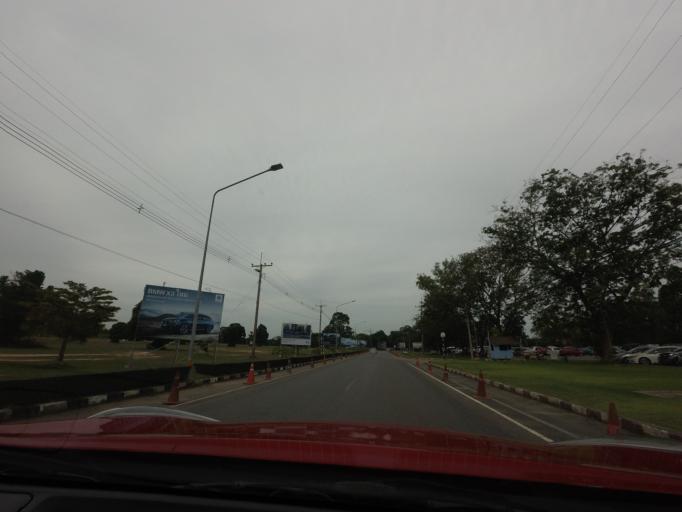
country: TH
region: Songkhla
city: Khlong Hoi Khong
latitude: 6.9382
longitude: 100.3946
